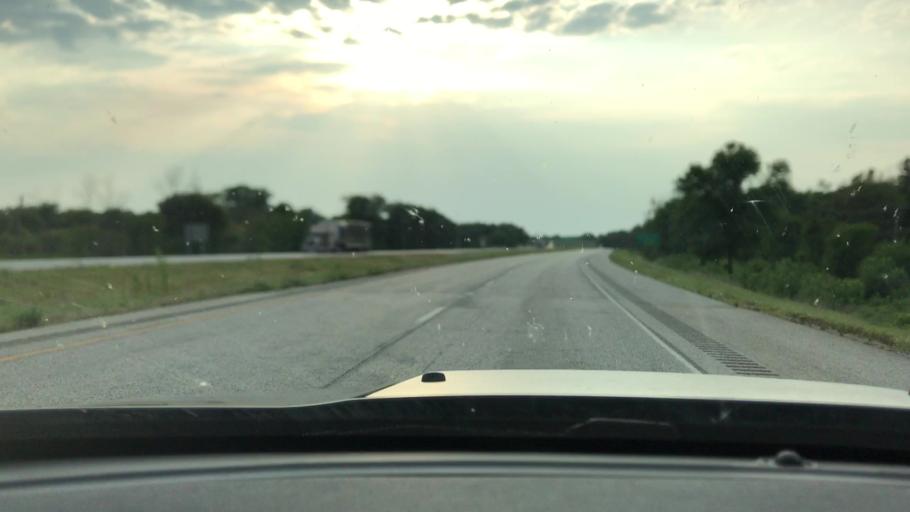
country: US
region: Illinois
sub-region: Rock Island County
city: Coal Valley
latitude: 41.4550
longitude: -90.4821
